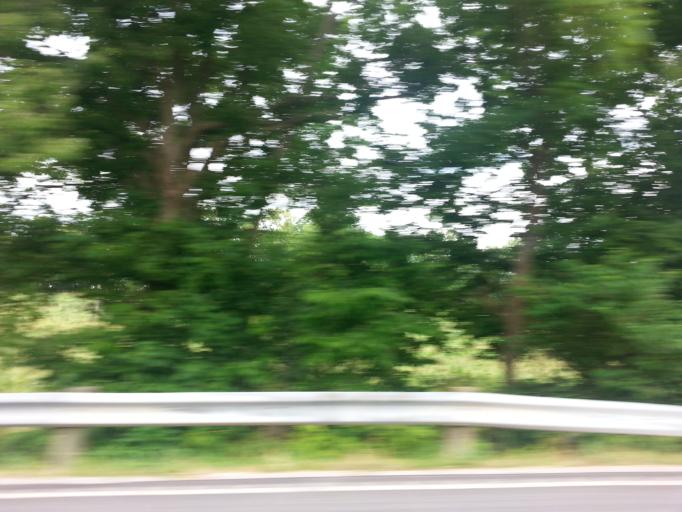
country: US
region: Kentucky
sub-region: Harrison County
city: Cynthiana
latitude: 38.4395
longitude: -84.2486
